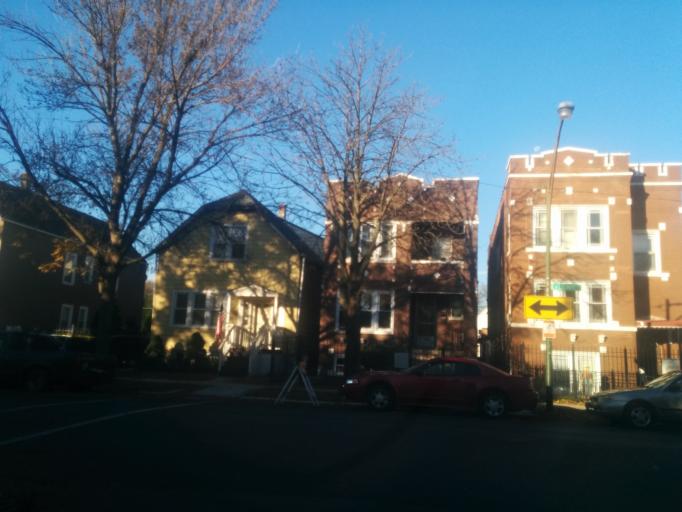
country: US
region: Illinois
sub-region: Cook County
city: Oak Park
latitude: 41.9268
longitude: -87.7610
